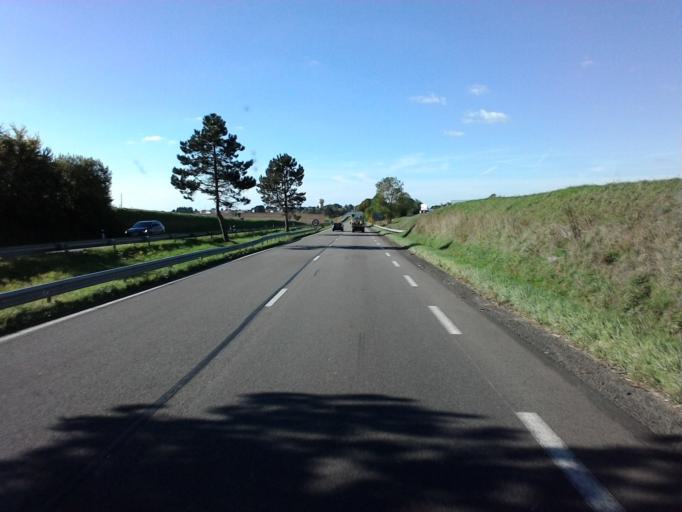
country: FR
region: Lorraine
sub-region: Departement de Meurthe-et-Moselle
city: Villers-la-Montagne
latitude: 49.4655
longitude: 5.8467
